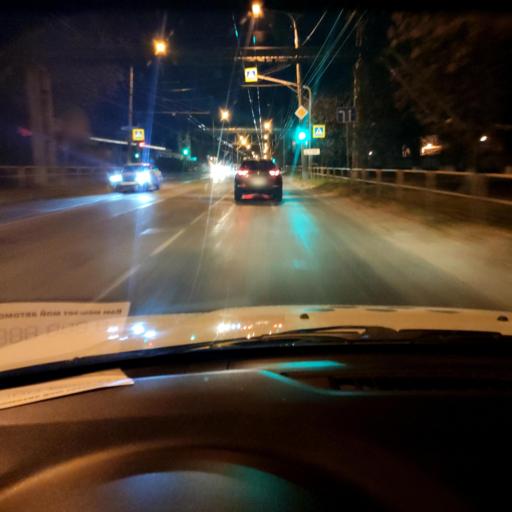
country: RU
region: Samara
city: Tol'yatti
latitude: 53.5437
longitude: 49.4450
